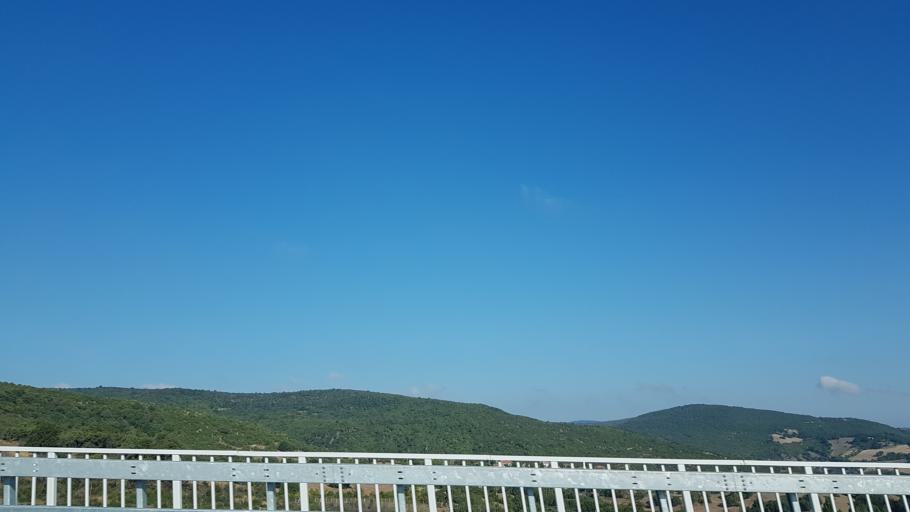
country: TR
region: Balikesir
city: Ertugrul
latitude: 39.5587
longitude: 27.7002
